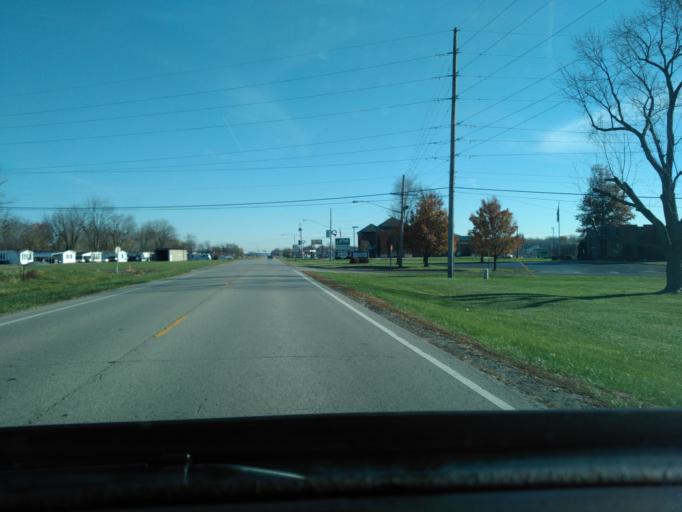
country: US
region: Illinois
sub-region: Bond County
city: Greenville
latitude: 38.8767
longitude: -89.3960
